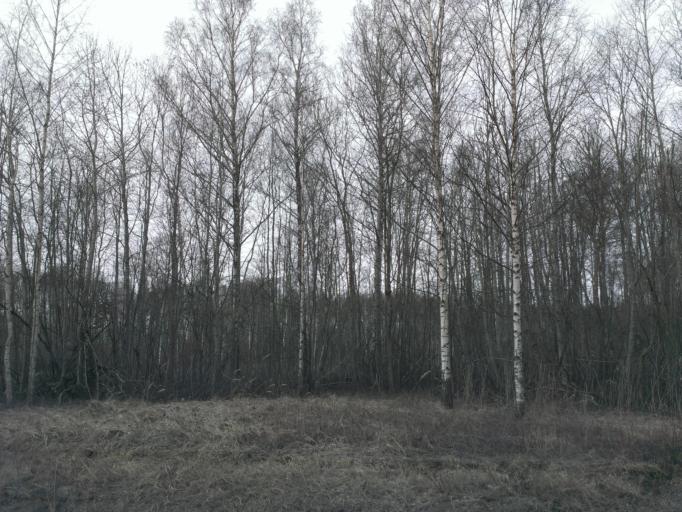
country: EE
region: Laeaene
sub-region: Lihula vald
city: Lihula
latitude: 58.6144
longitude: 23.5957
